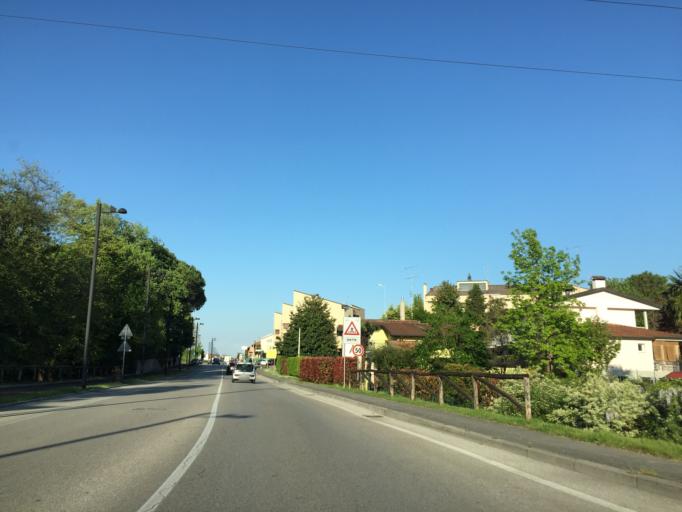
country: IT
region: Friuli Venezia Giulia
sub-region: Provincia di Pordenone
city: Porcia
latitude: 45.9572
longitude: 12.6201
